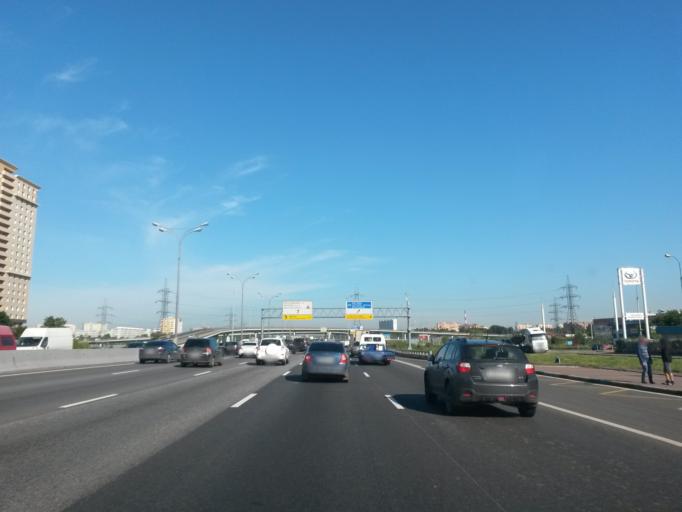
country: RU
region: Moscow
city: Babushkin
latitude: 55.8788
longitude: 37.7334
